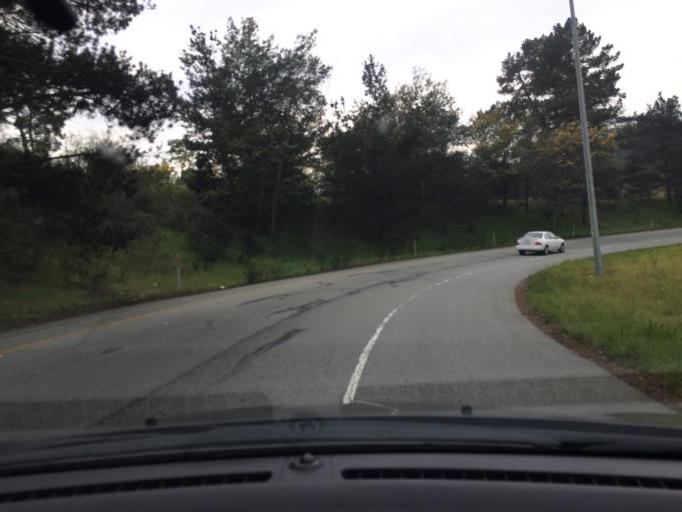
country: US
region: California
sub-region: Monterey County
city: Prunedale
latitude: 36.7889
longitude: -121.6663
